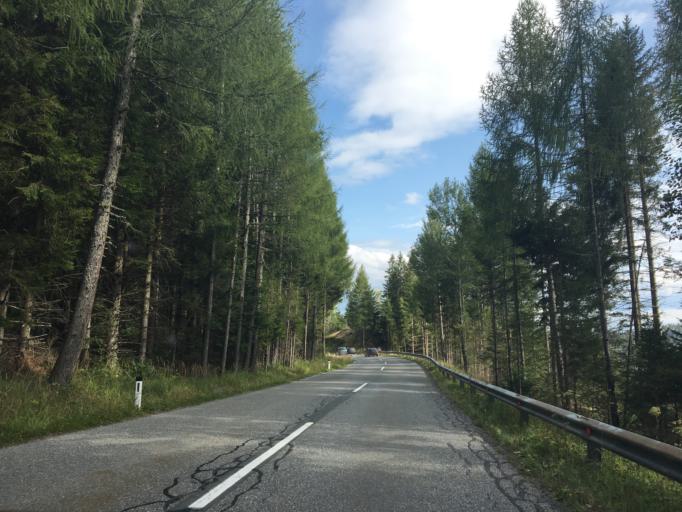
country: AT
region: Styria
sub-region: Politischer Bezirk Deutschlandsberg
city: Gressenberg
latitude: 46.8290
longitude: 15.0688
